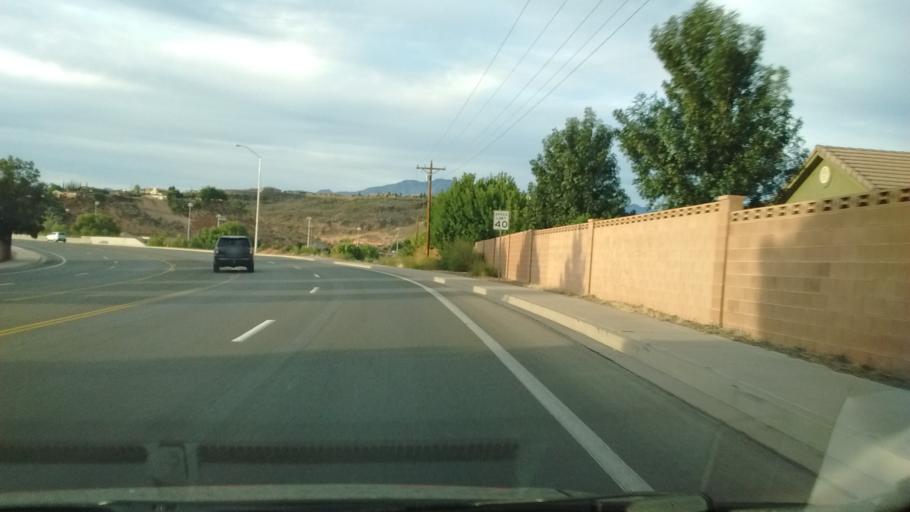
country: US
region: Utah
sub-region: Washington County
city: Washington
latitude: 37.1149
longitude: -113.5001
